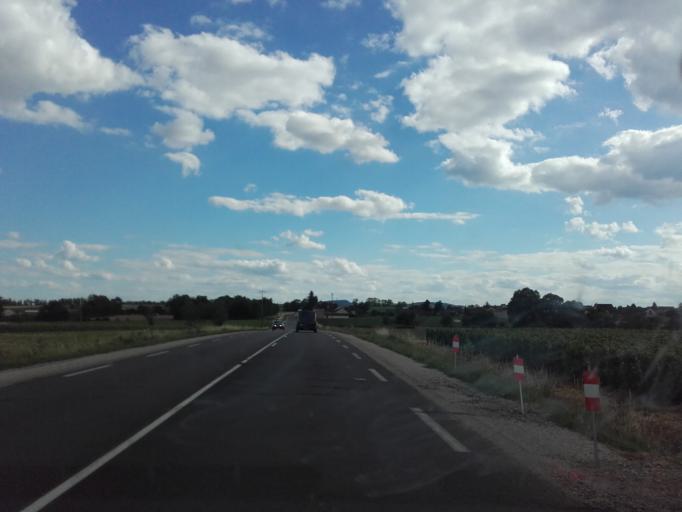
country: FR
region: Bourgogne
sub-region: Departement de la Cote-d'Or
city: Corpeau
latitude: 46.9487
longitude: 4.7632
